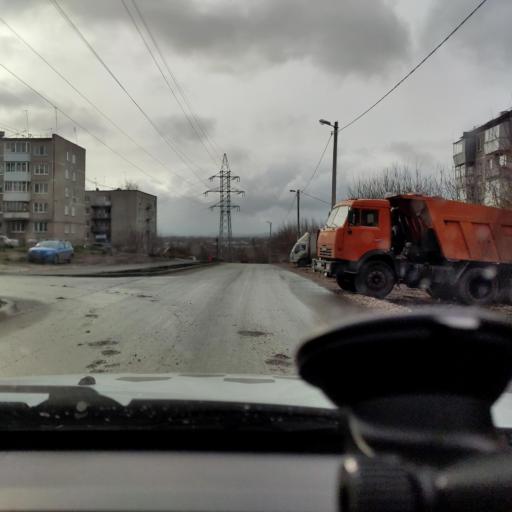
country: RU
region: Perm
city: Kondratovo
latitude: 57.9604
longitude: 56.1489
